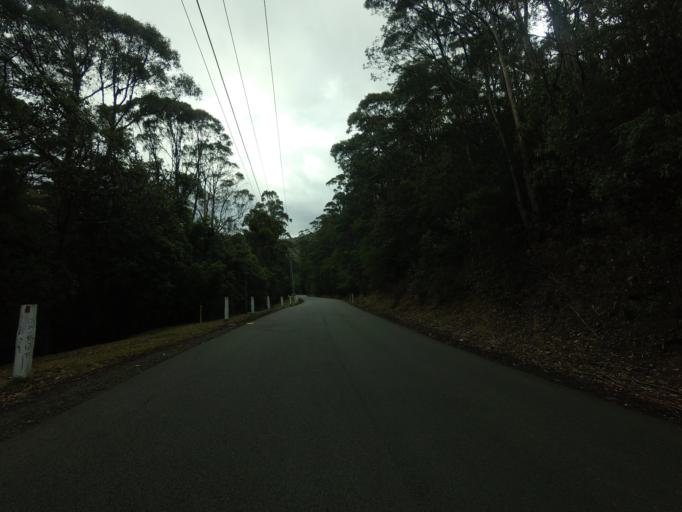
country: AU
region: Tasmania
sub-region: Hobart
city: Dynnyrne
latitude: -42.9067
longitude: 147.2670
